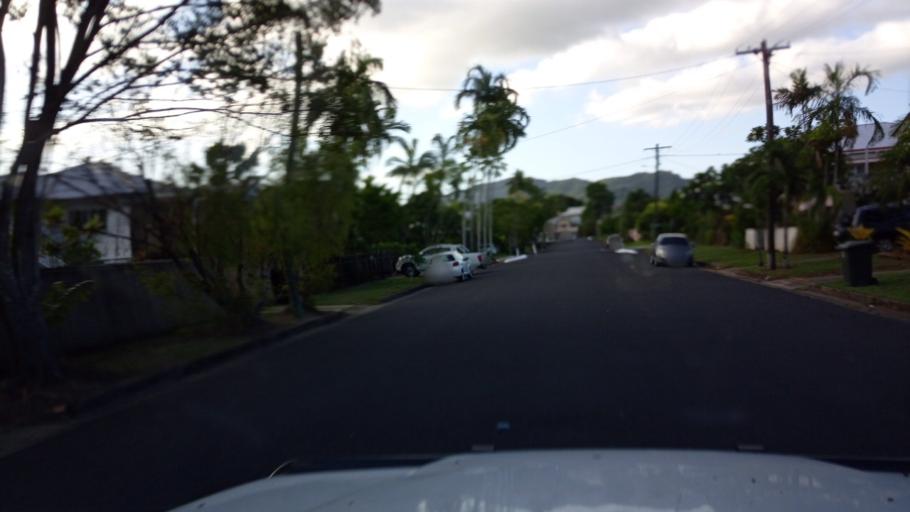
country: AU
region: Queensland
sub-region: Cairns
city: Cairns
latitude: -16.9172
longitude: 145.7594
